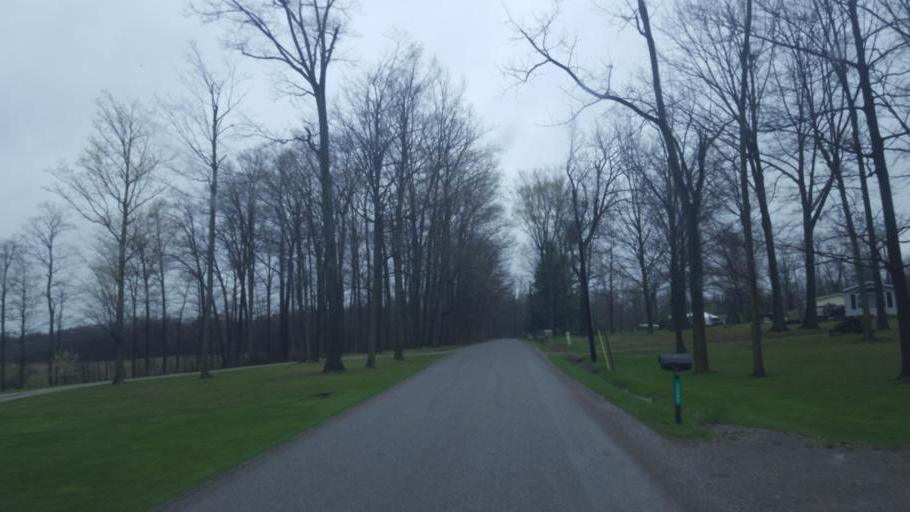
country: US
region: Ohio
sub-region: Morrow County
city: Mount Gilead
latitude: 40.4693
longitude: -82.8106
